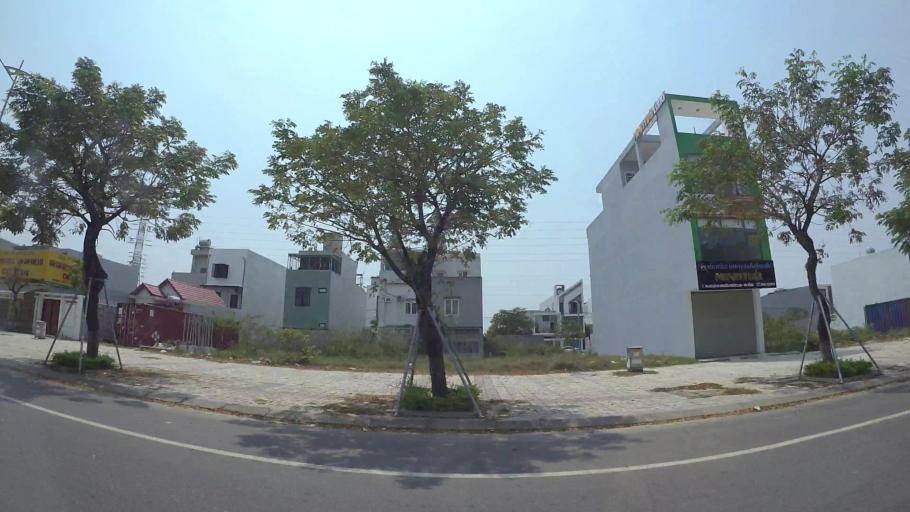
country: VN
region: Da Nang
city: Ngu Hanh Son
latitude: 16.0167
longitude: 108.2330
